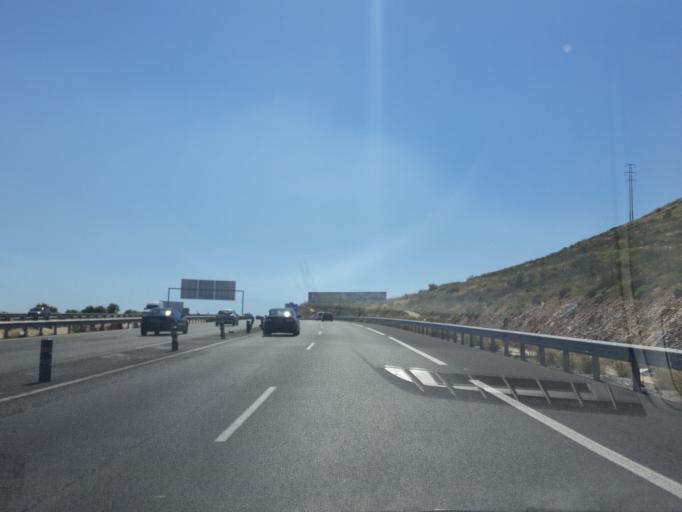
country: ES
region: Andalusia
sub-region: Provincia de Malaga
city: Torremolinos
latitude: 36.6236
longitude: -4.5173
